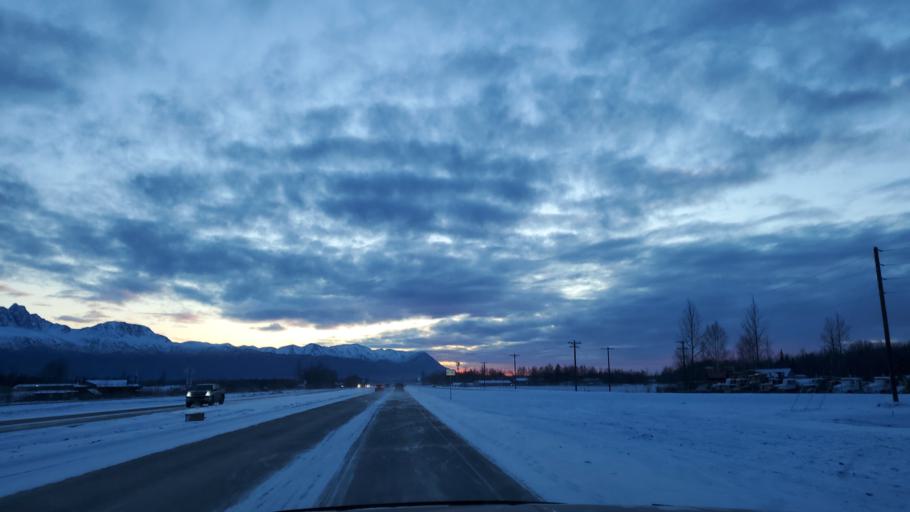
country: US
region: Alaska
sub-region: Matanuska-Susitna Borough
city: Palmer
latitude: 61.5847
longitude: -149.1314
